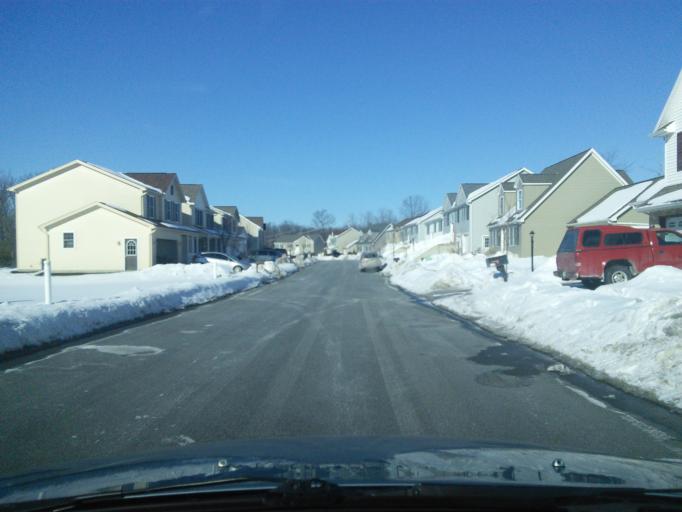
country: US
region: Pennsylvania
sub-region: Centre County
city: Park Forest Village
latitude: 40.8131
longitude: -77.9316
